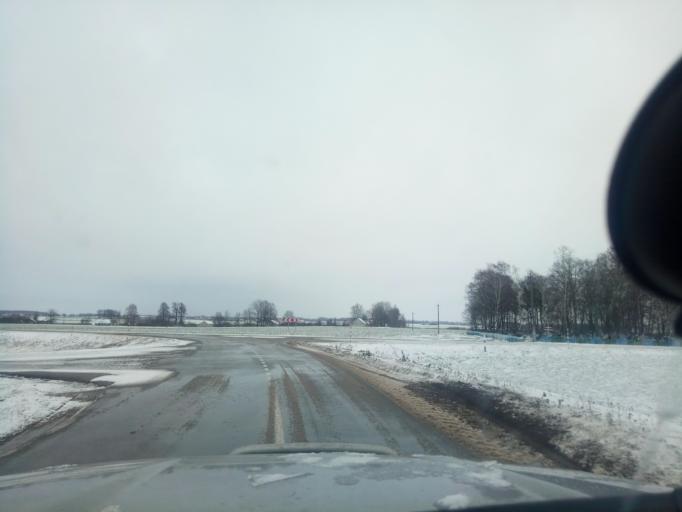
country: BY
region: Minsk
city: Klyetsk
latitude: 53.0396
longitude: 26.7472
